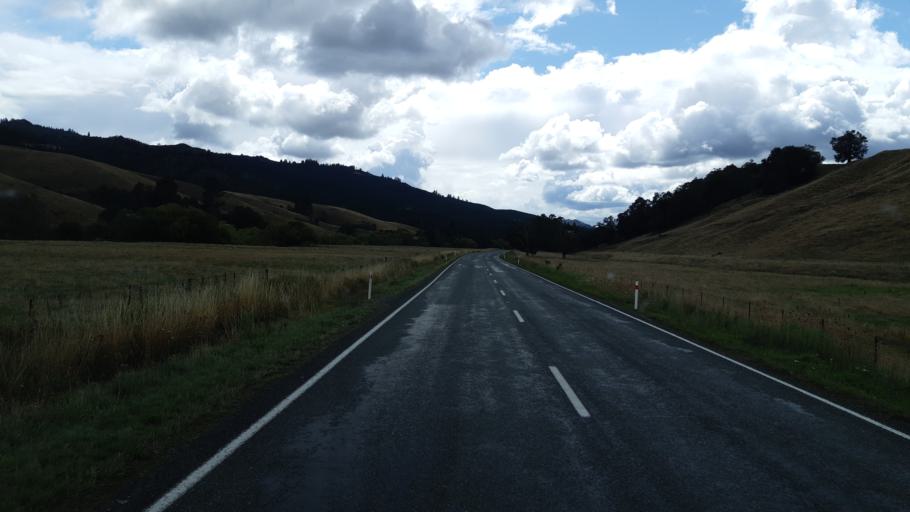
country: NZ
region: Tasman
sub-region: Tasman District
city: Wakefield
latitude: -41.5698
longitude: 172.7762
